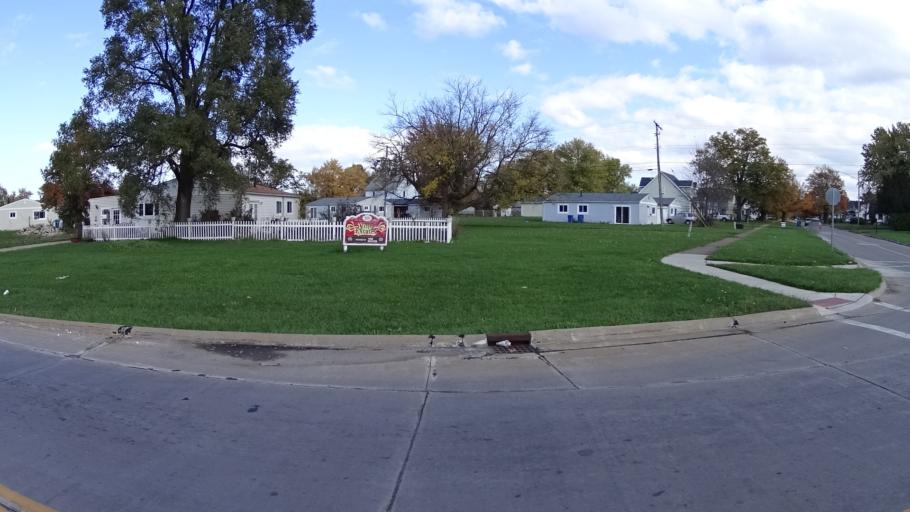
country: US
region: Ohio
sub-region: Lorain County
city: Lorain
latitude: 41.4389
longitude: -82.1465
